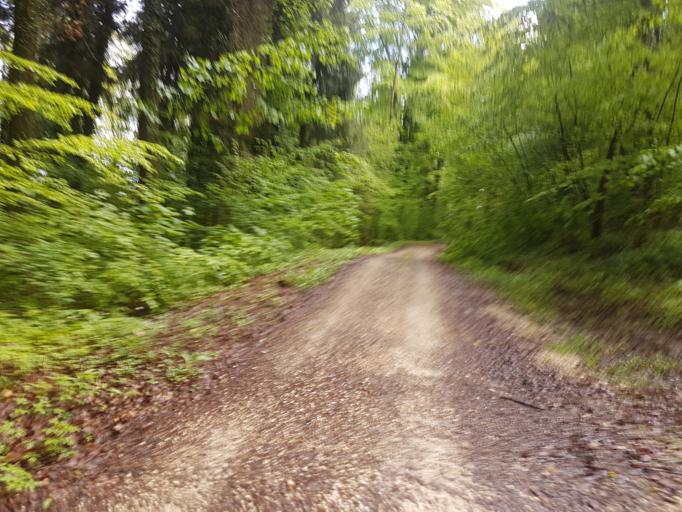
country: CH
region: Vaud
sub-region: Ouest Lausannois District
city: Bussigny
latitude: 46.5562
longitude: 6.5278
